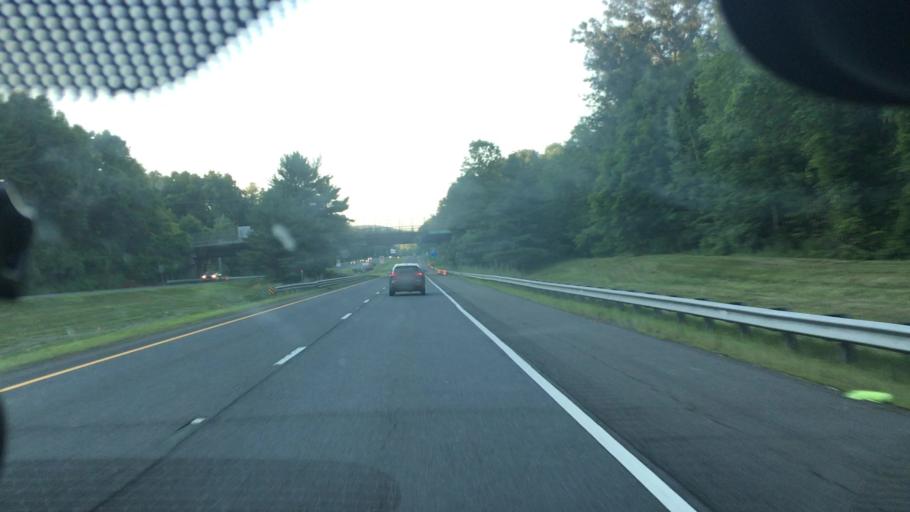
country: US
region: Massachusetts
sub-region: Franklin County
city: Greenfield
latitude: 42.5918
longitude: -72.6189
